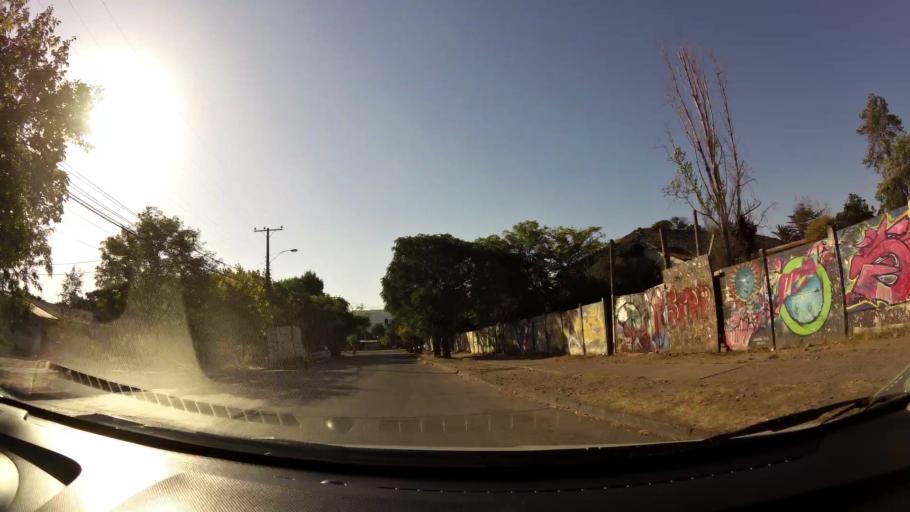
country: CL
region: Maule
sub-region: Provincia de Talca
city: Talca
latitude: -35.4357
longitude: -71.6791
